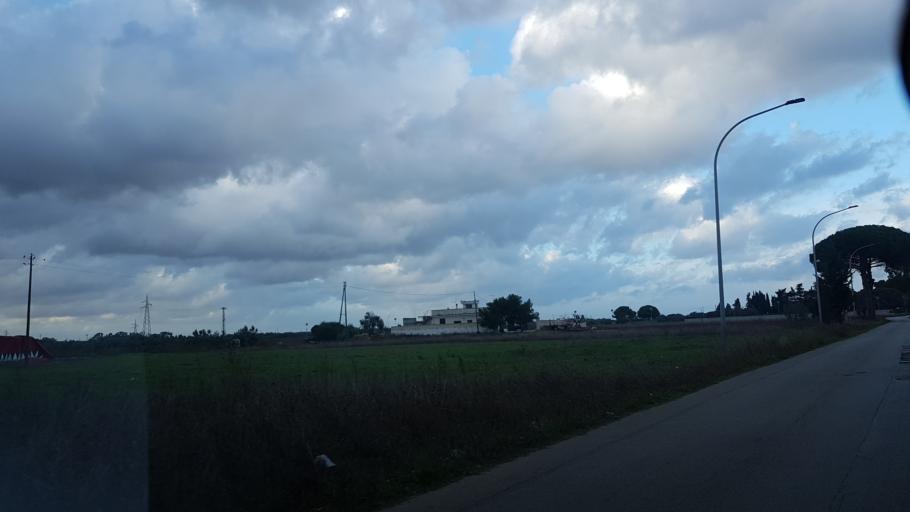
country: IT
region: Apulia
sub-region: Provincia di Brindisi
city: San Pietro Vernotico
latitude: 40.4960
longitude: 18.0022
